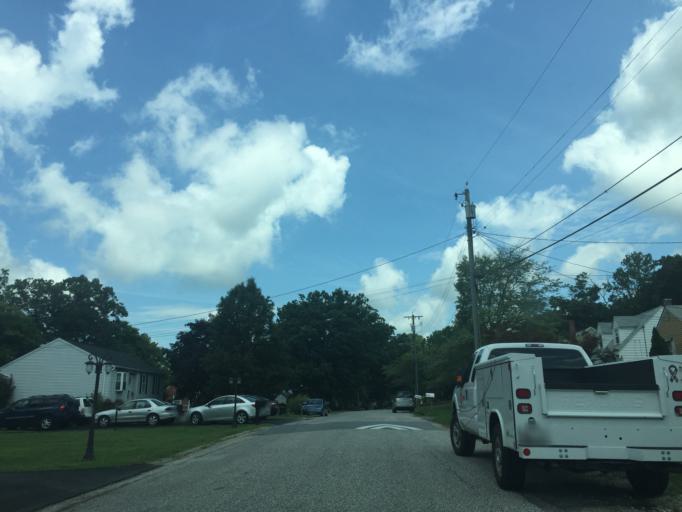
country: US
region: Maryland
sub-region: Baltimore County
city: Carney
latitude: 39.3970
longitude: -76.5128
